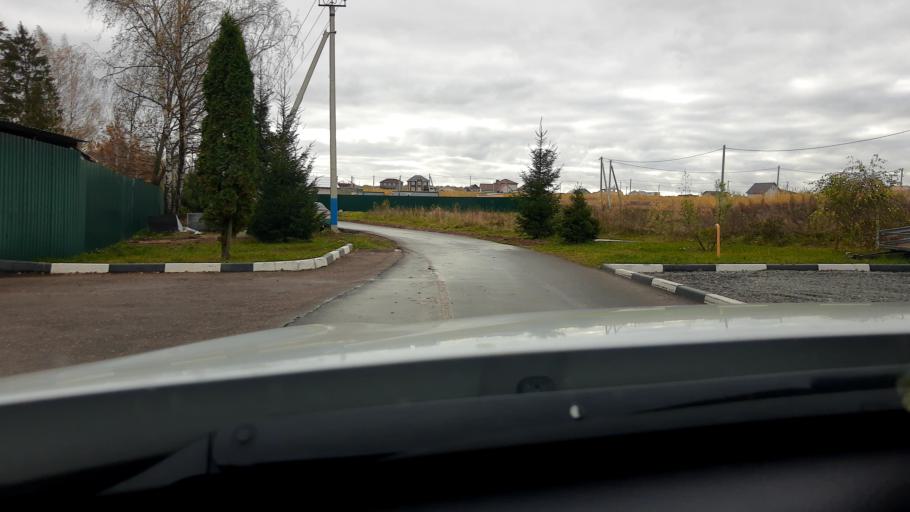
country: RU
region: Moskovskaya
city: Annino
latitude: 55.5612
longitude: 37.2521
